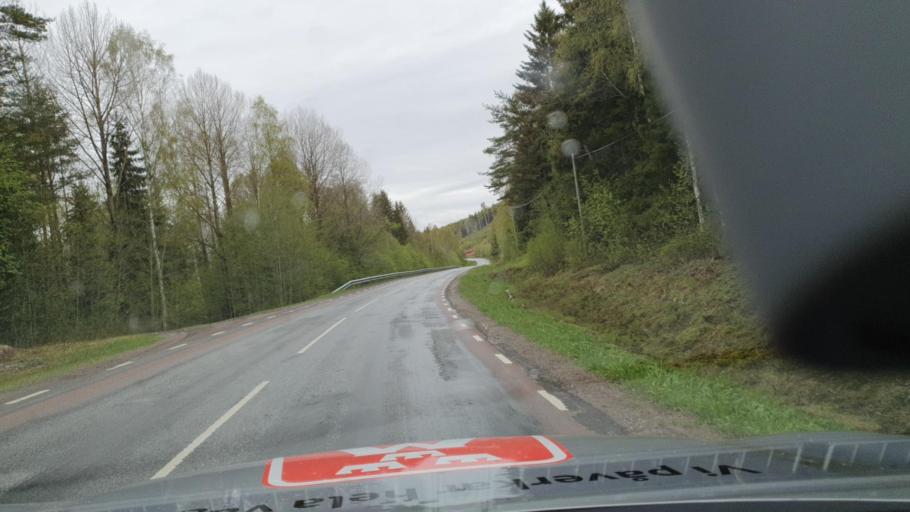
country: SE
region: Vaesternorrland
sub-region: OErnskoeldsviks Kommun
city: Bjasta
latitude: 63.3672
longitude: 18.4959
